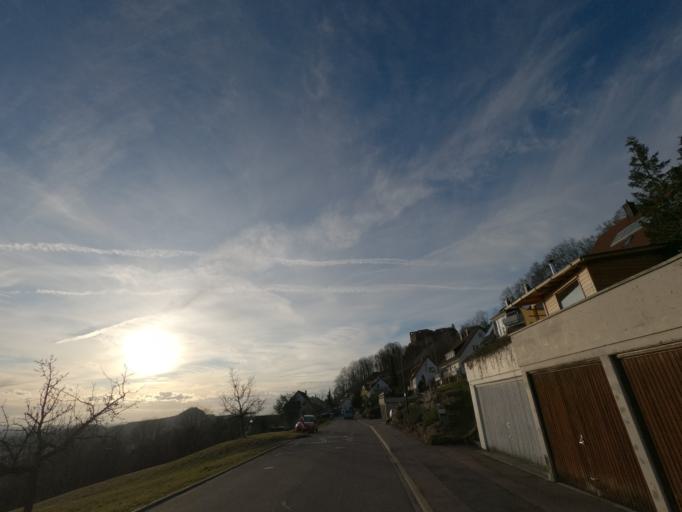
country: DE
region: Baden-Wuerttemberg
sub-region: Regierungsbezirk Stuttgart
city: Waldstetten
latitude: 48.7545
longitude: 9.7859
